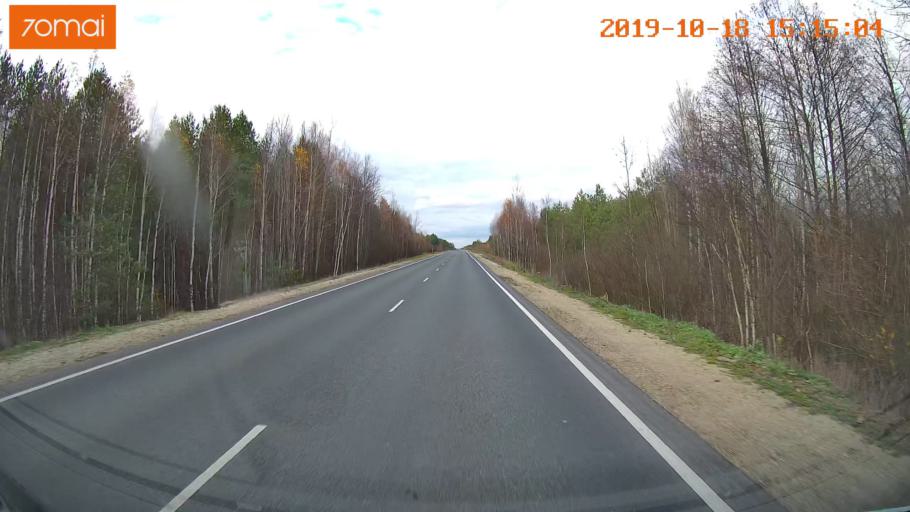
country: RU
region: Vladimir
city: Gus'-Khrustal'nyy
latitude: 55.6129
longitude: 40.7216
